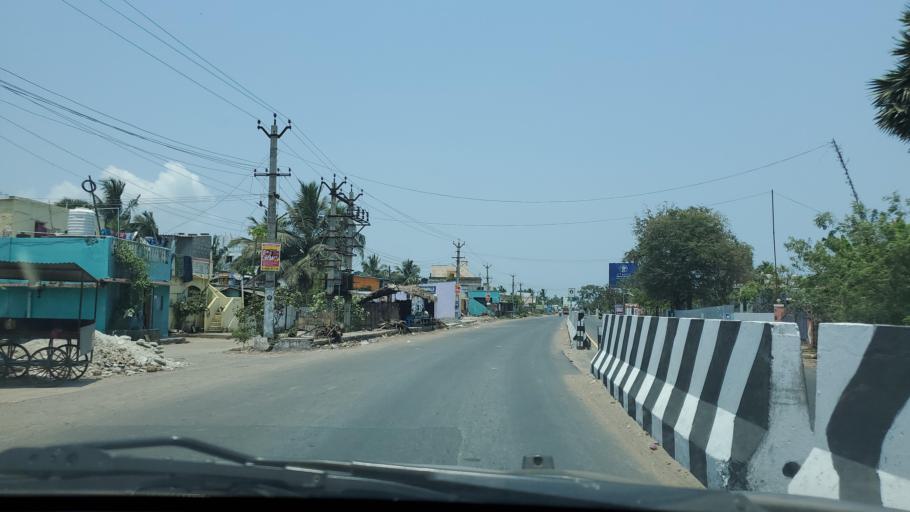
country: IN
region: Tamil Nadu
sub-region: Kancheepuram
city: Vengavasal
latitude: 12.8589
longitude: 80.1726
